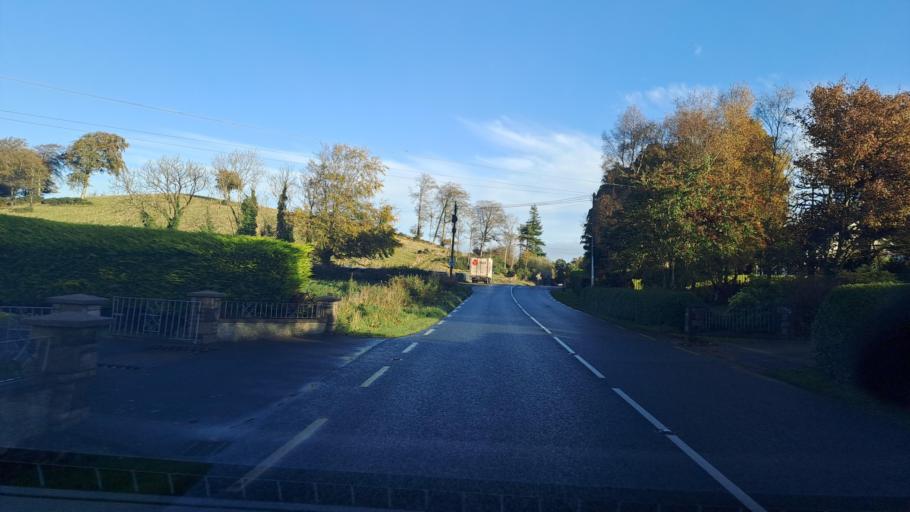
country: IE
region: Ulster
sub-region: County Monaghan
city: Monaghan
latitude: 54.2120
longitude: -6.9850
